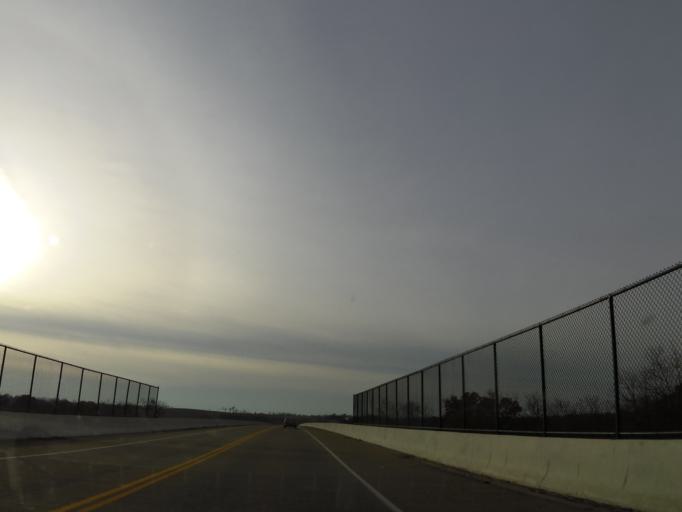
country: US
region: Kentucky
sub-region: Harrison County
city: Cynthiana
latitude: 38.3998
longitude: -84.2957
